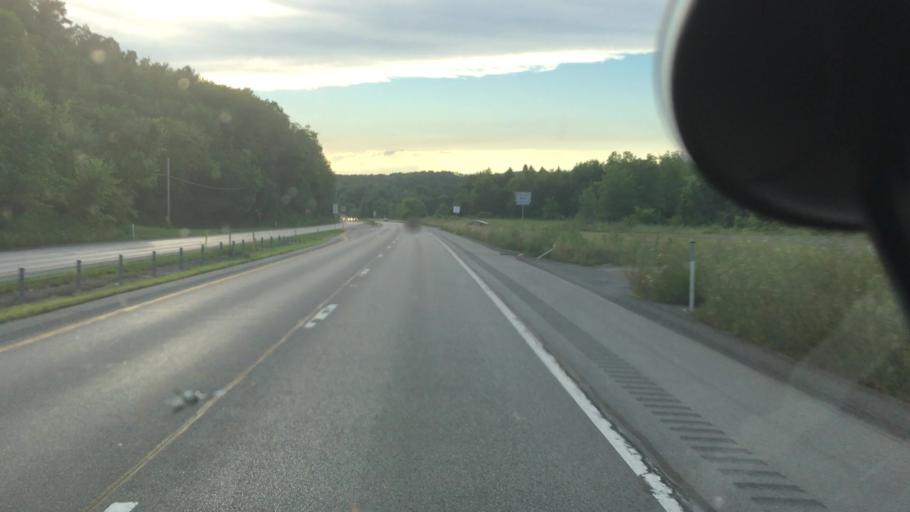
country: US
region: Pennsylvania
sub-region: Beaver County
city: Big Beaver
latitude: 40.7902
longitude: -80.4090
